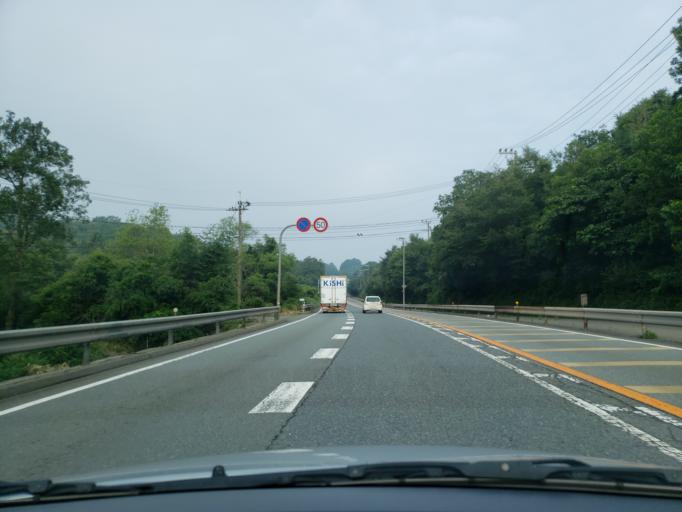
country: JP
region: Hyogo
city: Kariya
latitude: 34.8428
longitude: 134.3347
